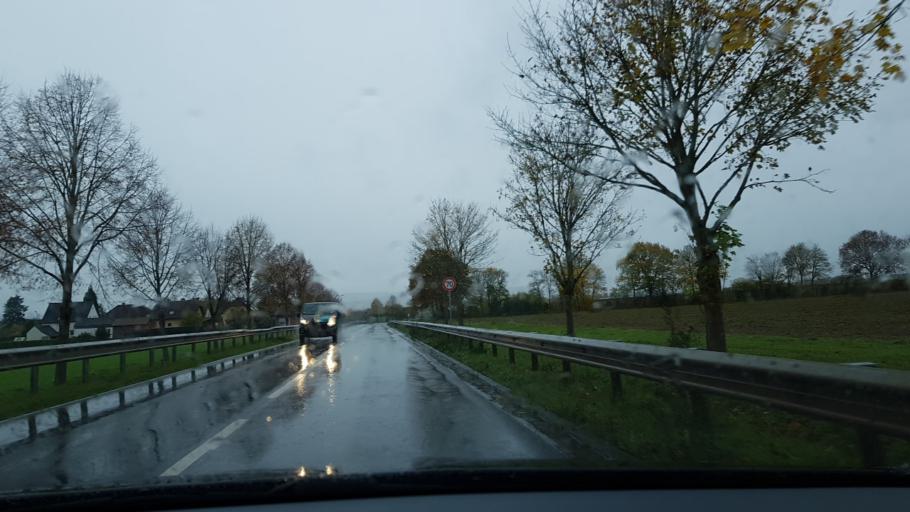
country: DE
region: Rheinland-Pfalz
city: Neuerburg
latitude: 49.9832
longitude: 6.9378
